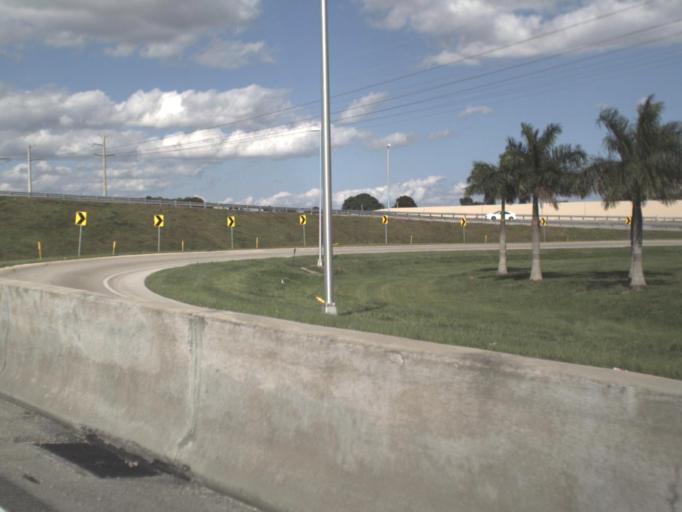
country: US
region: Florida
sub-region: Broward County
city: Lauderhill
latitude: 26.1388
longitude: -80.2190
